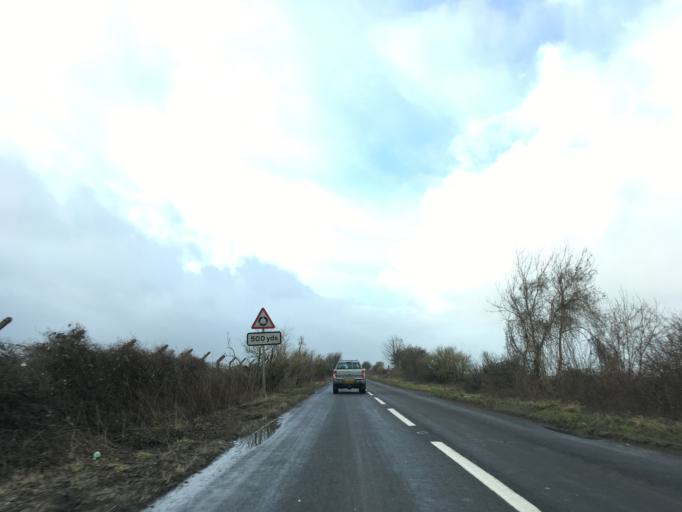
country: GB
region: England
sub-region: Gloucestershire
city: Chalford
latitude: 51.7151
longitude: -2.1221
